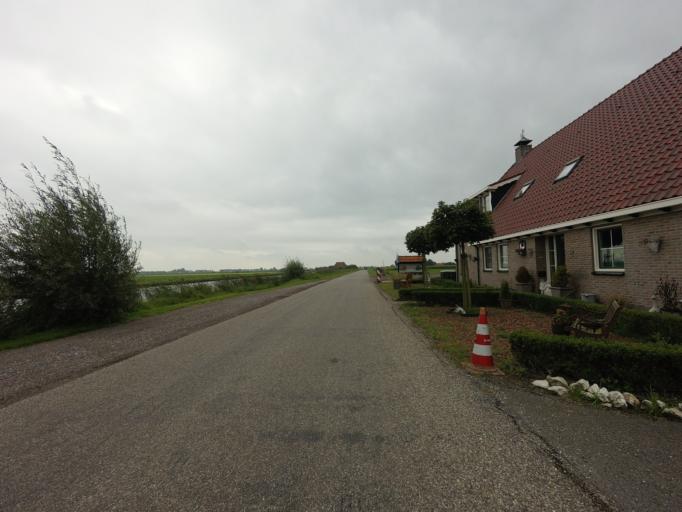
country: NL
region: Friesland
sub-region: Sudwest Fryslan
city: Workum
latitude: 52.9978
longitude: 5.4745
